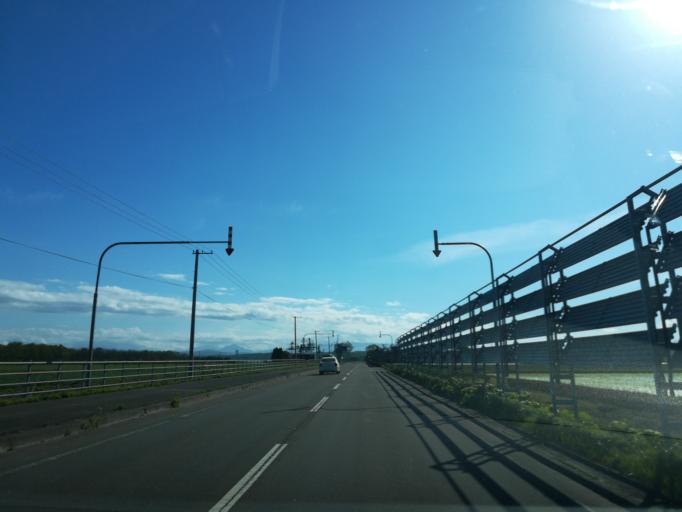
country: JP
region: Hokkaido
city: Kitahiroshima
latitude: 43.0422
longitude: 141.5871
